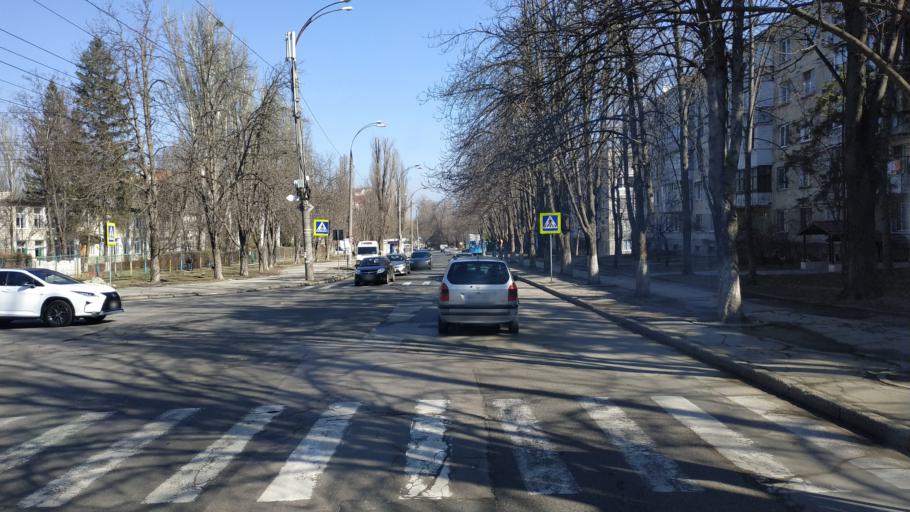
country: MD
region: Chisinau
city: Vatra
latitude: 47.0307
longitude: 28.7903
